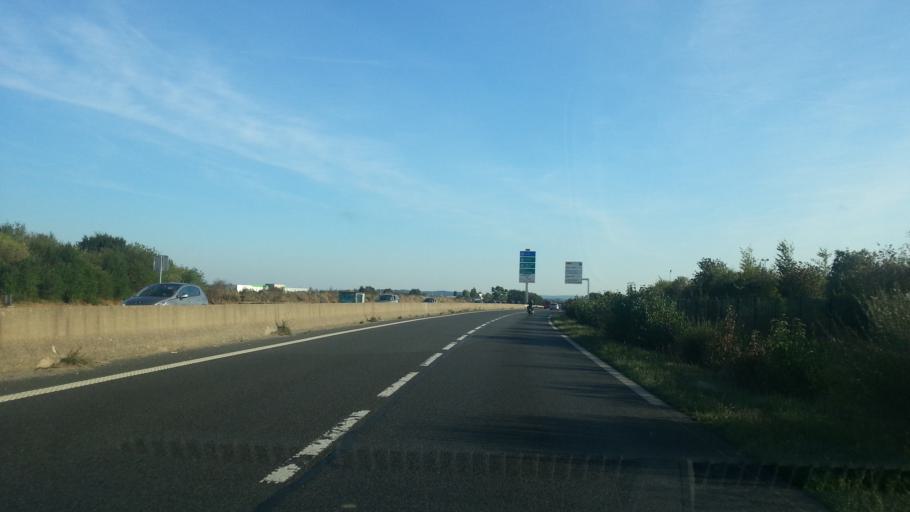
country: FR
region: Picardie
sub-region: Departement de l'Oise
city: Tille
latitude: 49.4426
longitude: 2.1117
